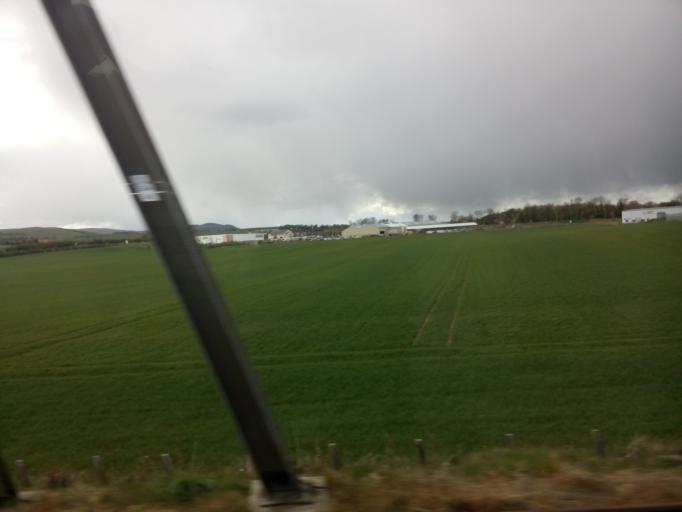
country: GB
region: Scotland
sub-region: East Lothian
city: Dunbar
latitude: 55.9929
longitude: -2.5046
